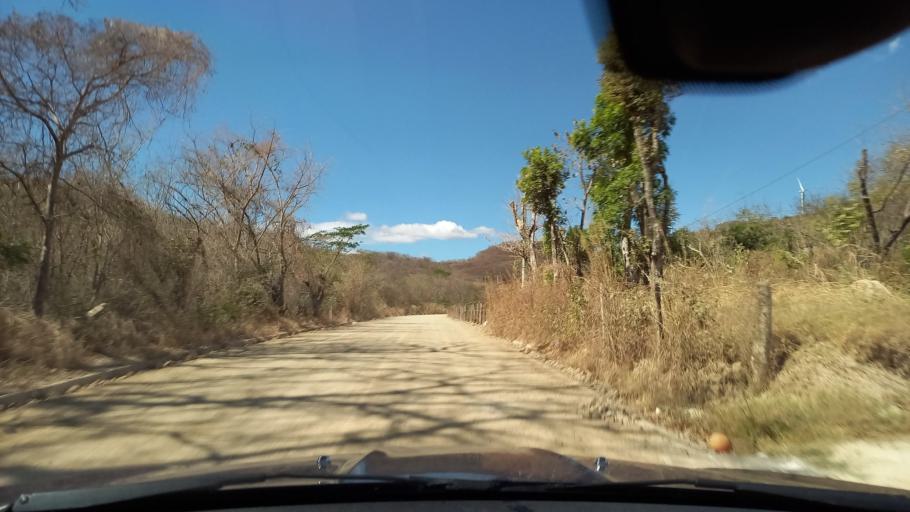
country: SV
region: Santa Ana
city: Metapan
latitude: 14.3602
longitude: -89.4716
